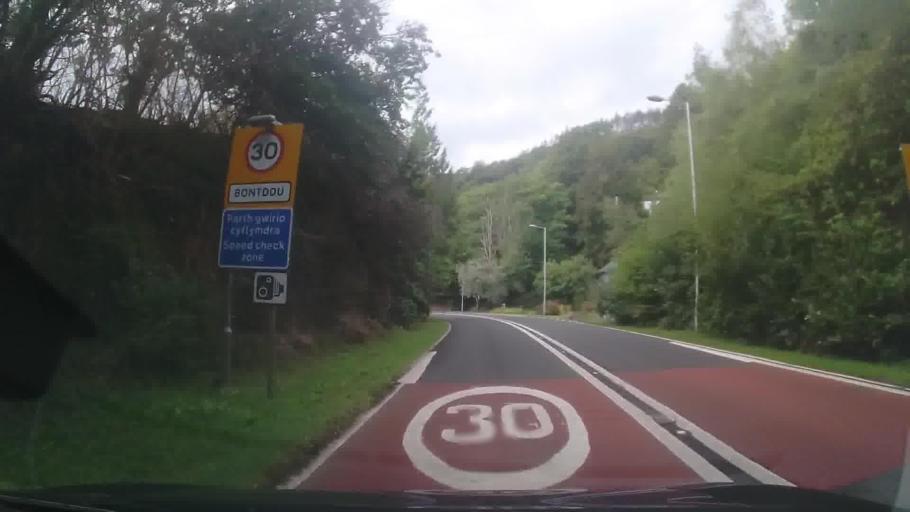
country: GB
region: Wales
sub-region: Gwynedd
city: Dolgellau
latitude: 52.7508
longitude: -3.9613
